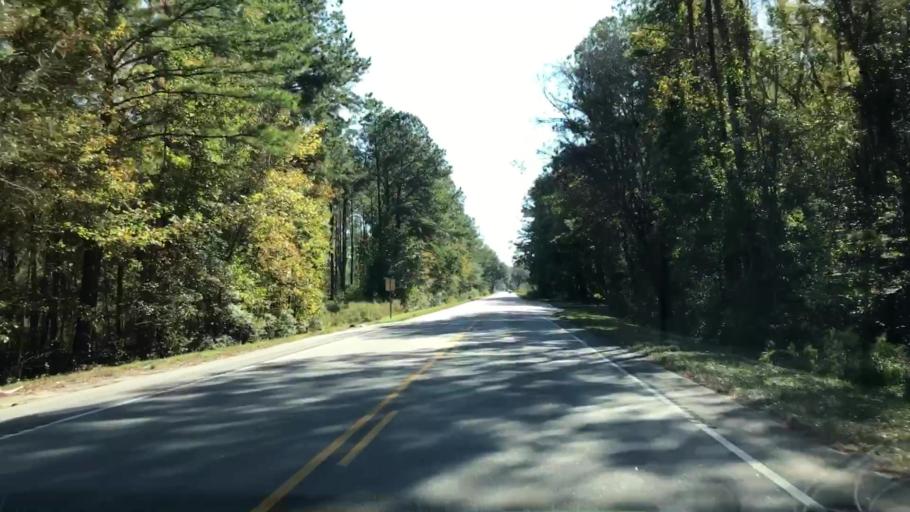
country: US
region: South Carolina
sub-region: Jasper County
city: Ridgeland
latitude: 32.5767
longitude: -80.9274
